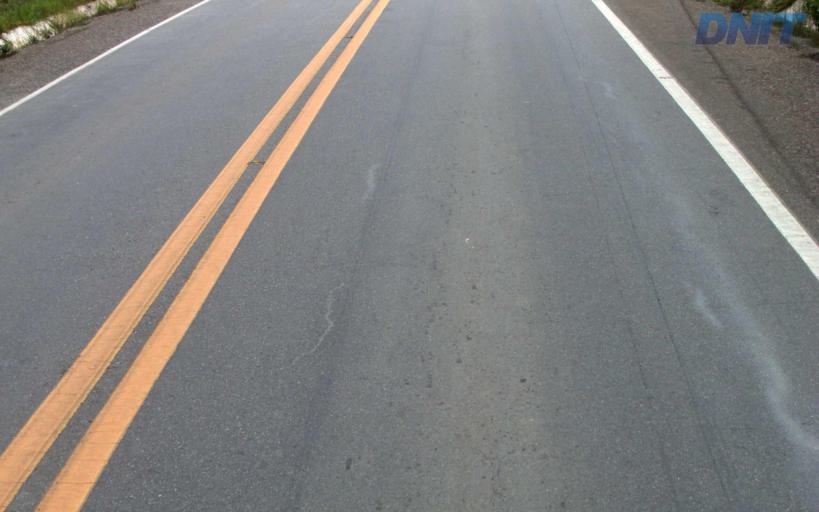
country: BR
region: Minas Gerais
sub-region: Governador Valadares
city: Governador Valadares
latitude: -19.0218
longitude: -42.1440
